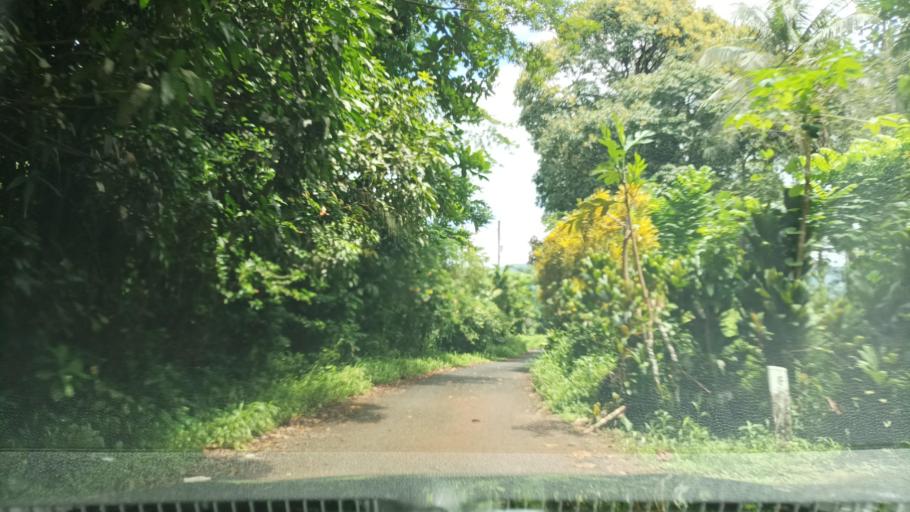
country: FM
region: Pohnpei
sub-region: Kolonia Municipality
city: Kolonia
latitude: 6.9619
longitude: 158.2235
